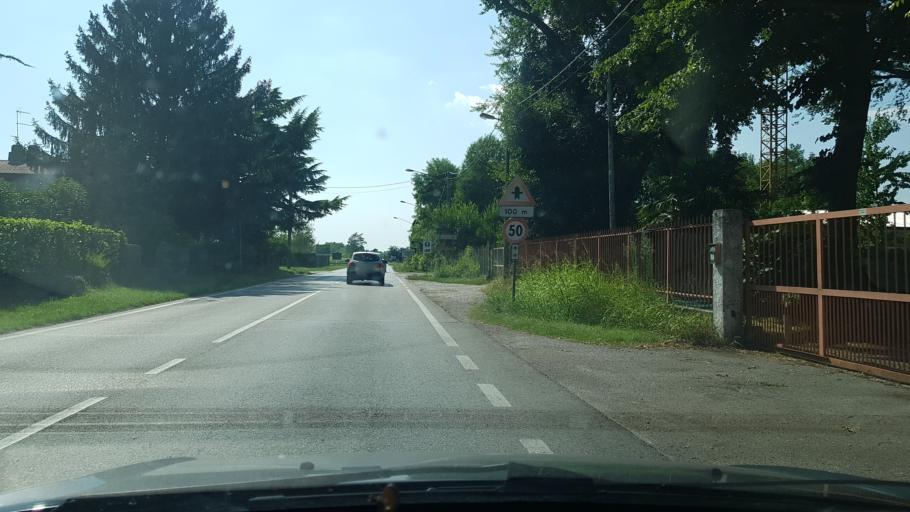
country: IT
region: Friuli Venezia Giulia
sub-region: Provincia di Gorizia
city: Staranzano
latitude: 45.7944
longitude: 13.5032
